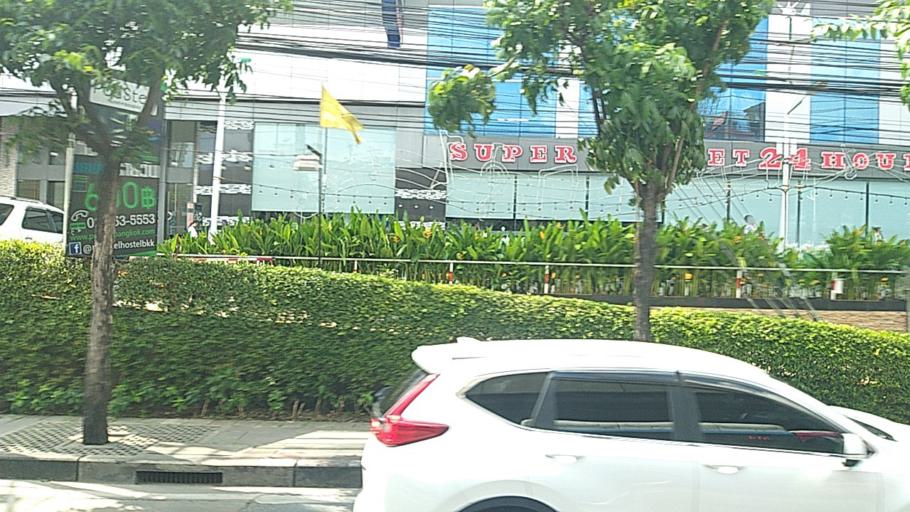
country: TH
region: Bangkok
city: Huai Khwang
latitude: 13.8039
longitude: 100.5746
